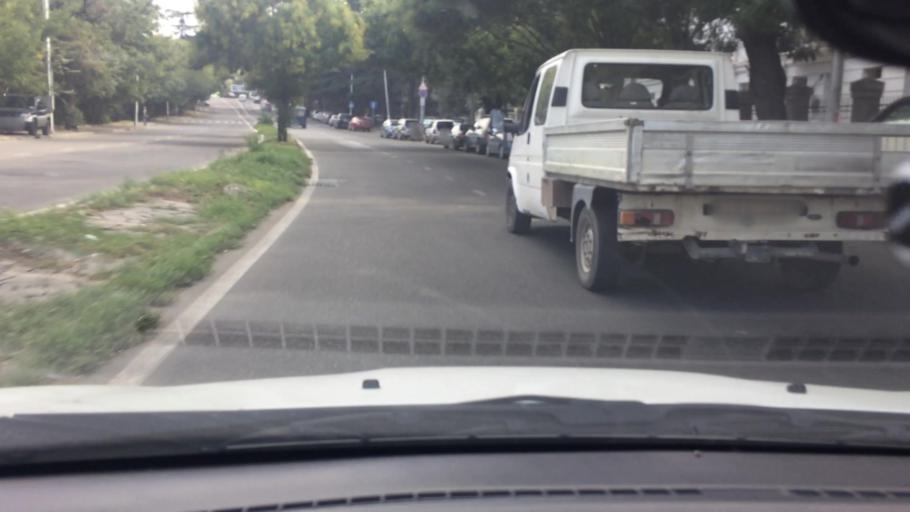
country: GE
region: T'bilisi
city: Tbilisi
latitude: 41.6736
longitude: 44.8317
